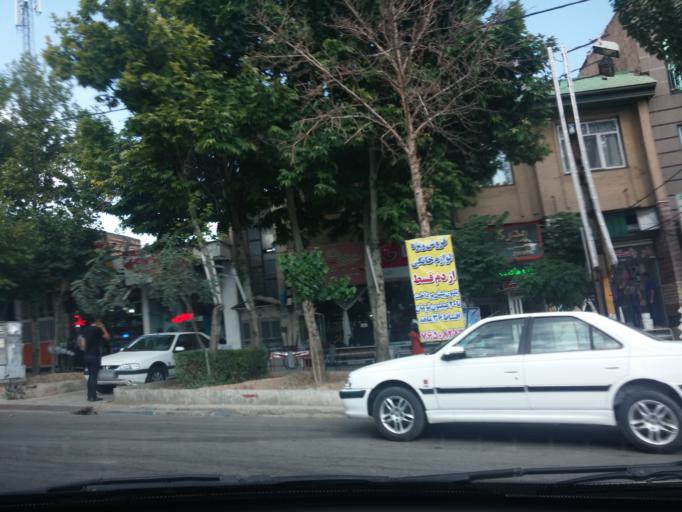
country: IR
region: Tehran
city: Damavand
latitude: 35.7334
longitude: 51.9067
